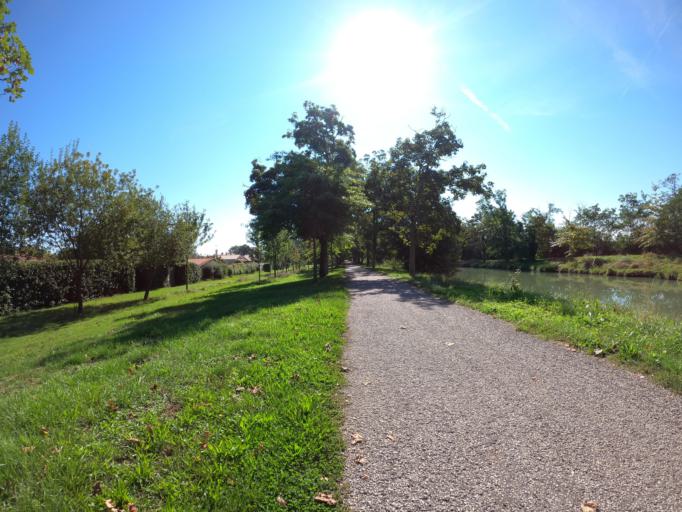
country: FR
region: Aquitaine
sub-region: Departement du Lot-et-Garonne
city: Bon-Encontre
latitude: 44.1861
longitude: 0.6538
